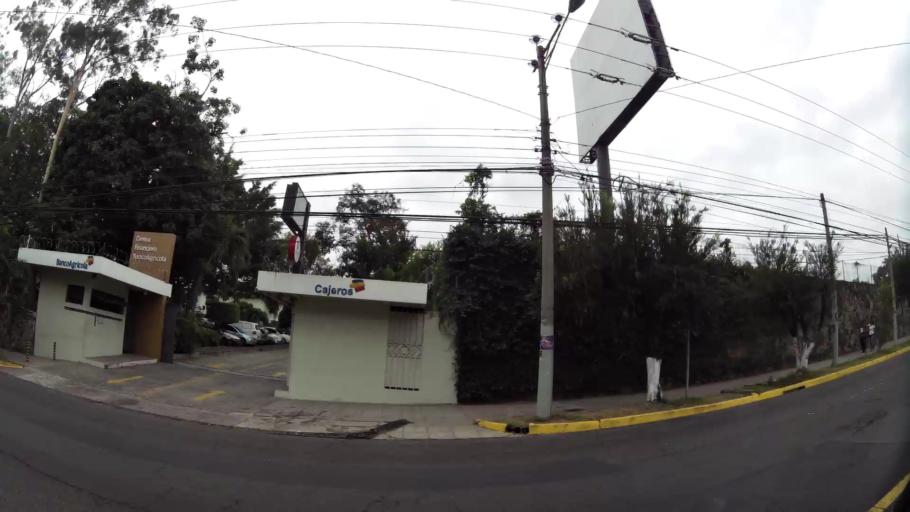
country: SV
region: San Salvador
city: Mejicanos
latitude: 13.7016
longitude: -89.2281
